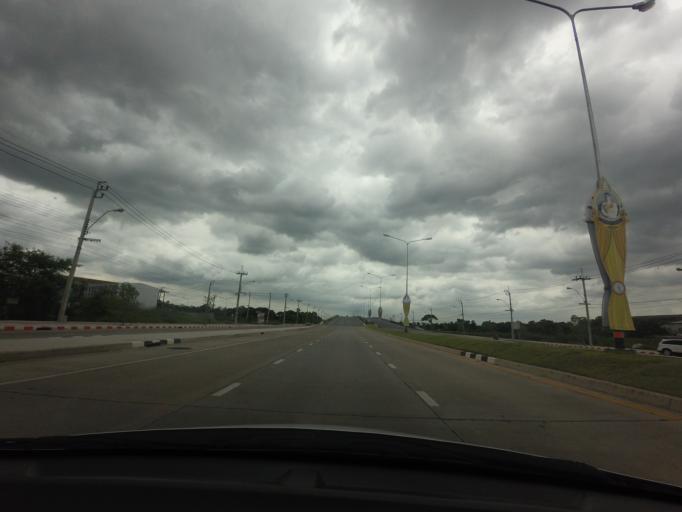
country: TH
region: Bangkok
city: Saphan Sung
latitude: 13.7545
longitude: 100.7207
